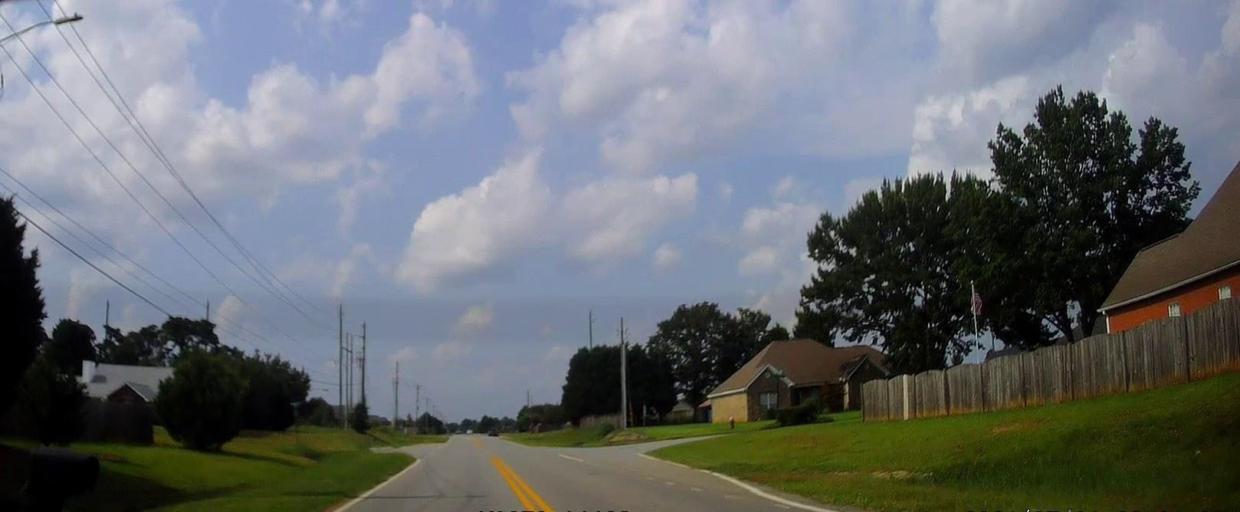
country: US
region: Georgia
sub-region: Houston County
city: Centerville
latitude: 32.5620
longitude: -83.6522
